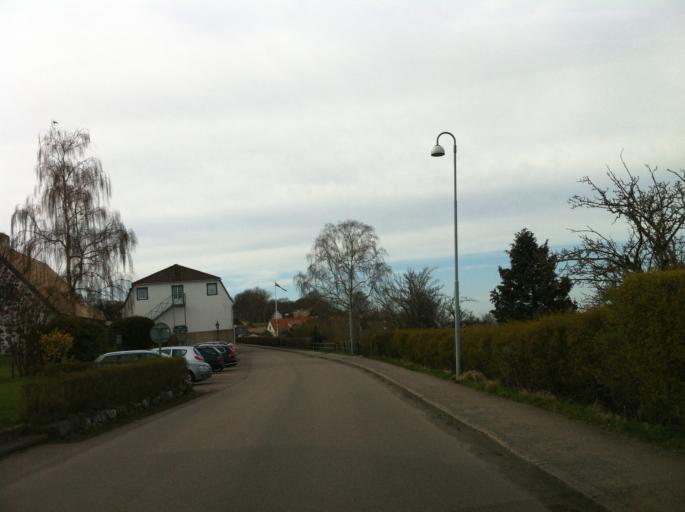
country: SE
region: Skane
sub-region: Hoganas Kommun
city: Hoganas
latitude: 56.2740
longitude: 12.5728
